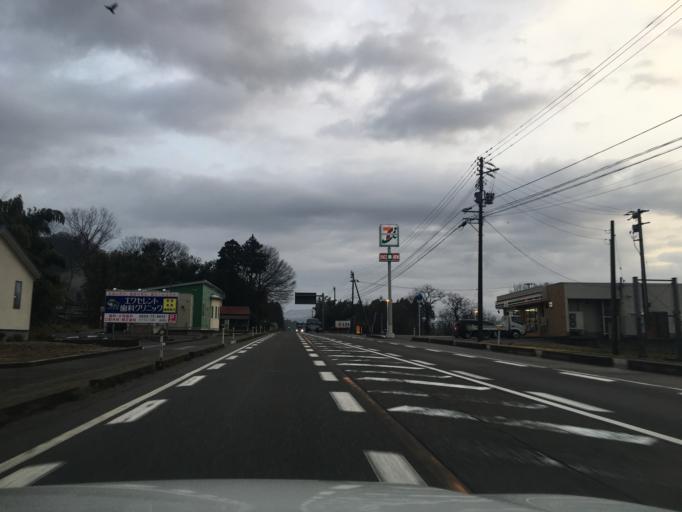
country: JP
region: Niigata
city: Murakami
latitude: 38.2839
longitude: 139.5227
